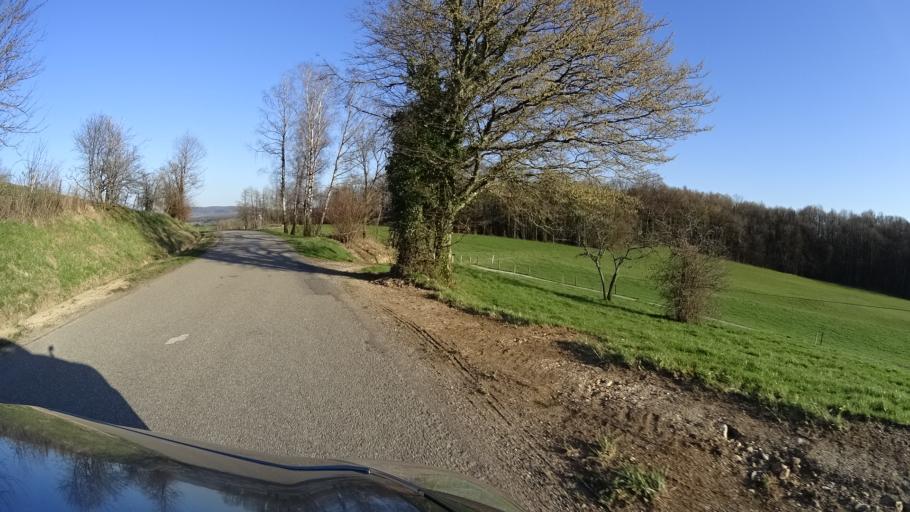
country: FR
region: Franche-Comte
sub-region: Departement du Doubs
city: Morre
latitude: 47.2064
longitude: 6.0526
